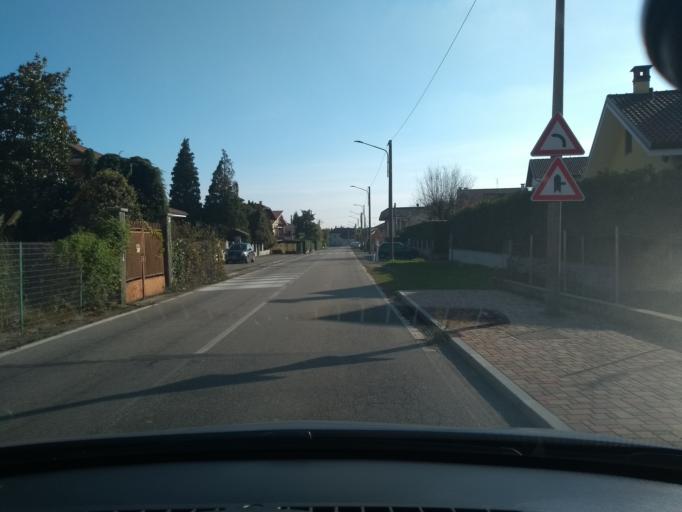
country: IT
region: Piedmont
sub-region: Provincia di Torino
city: Fiano
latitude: 45.2156
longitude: 7.5370
